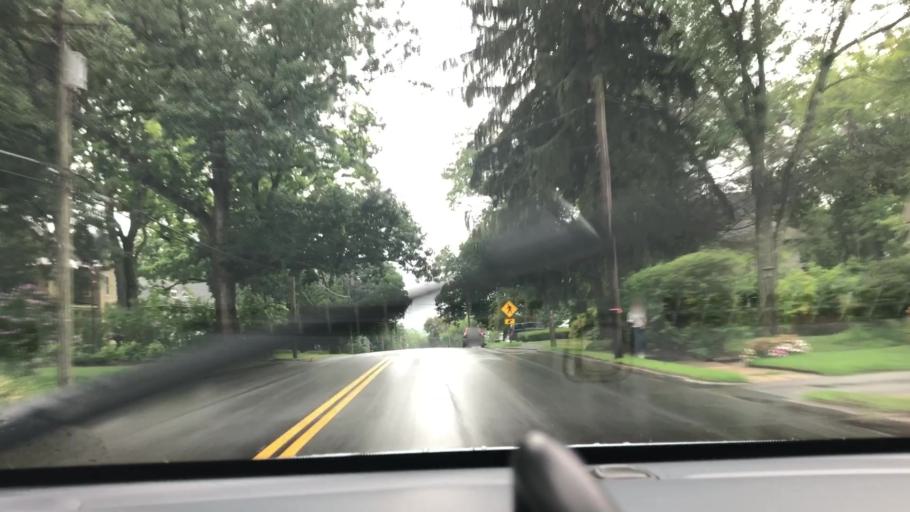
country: US
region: New Hampshire
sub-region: Hillsborough County
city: Manchester
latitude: 43.0153
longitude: -71.4617
